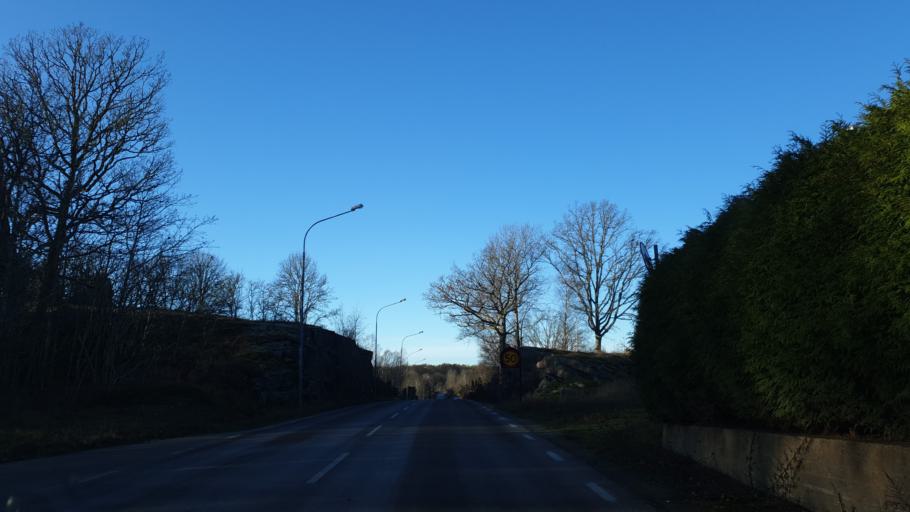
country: SE
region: Blekinge
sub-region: Ronneby Kommun
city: Ronneby
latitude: 56.1972
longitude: 15.3145
